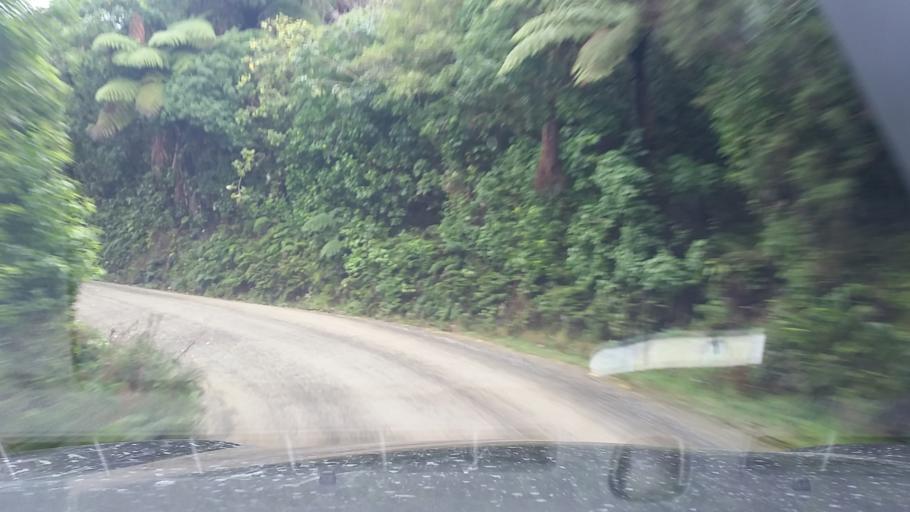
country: NZ
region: Marlborough
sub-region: Marlborough District
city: Picton
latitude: -41.1790
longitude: 173.9884
